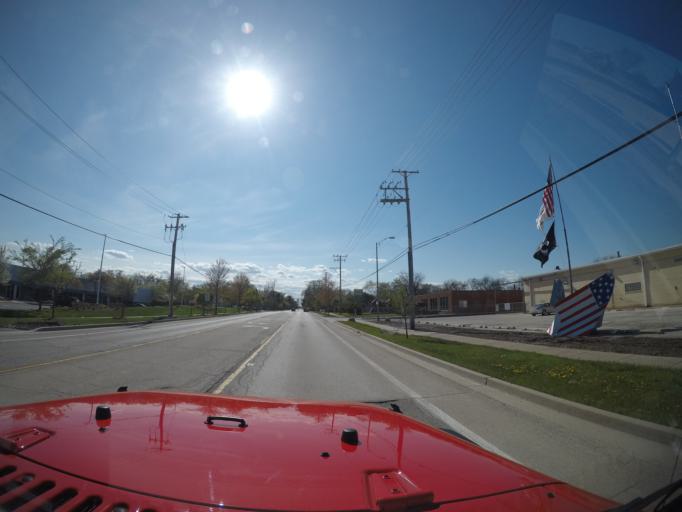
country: US
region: Illinois
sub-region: Cook County
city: Northbrook
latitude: 42.1165
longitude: -87.8274
